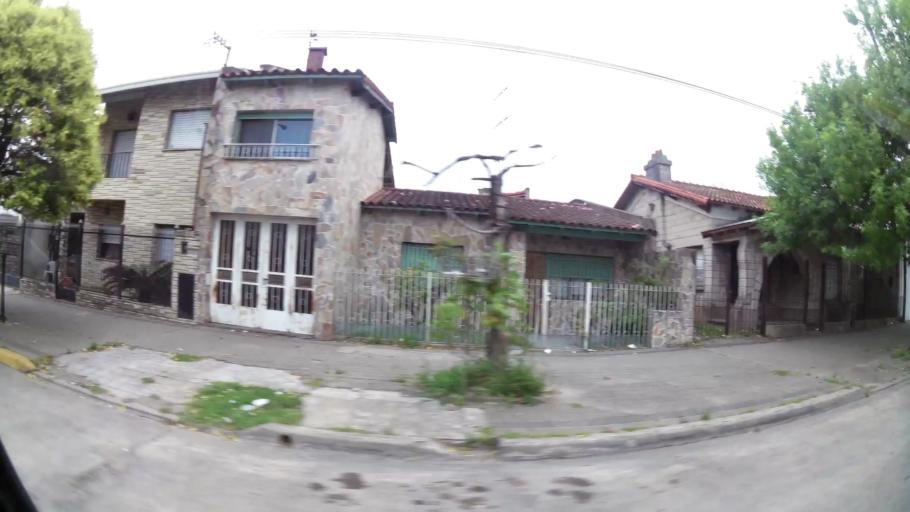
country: AR
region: Buenos Aires
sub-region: Partido de La Plata
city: La Plata
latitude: -34.9229
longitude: -57.9883
